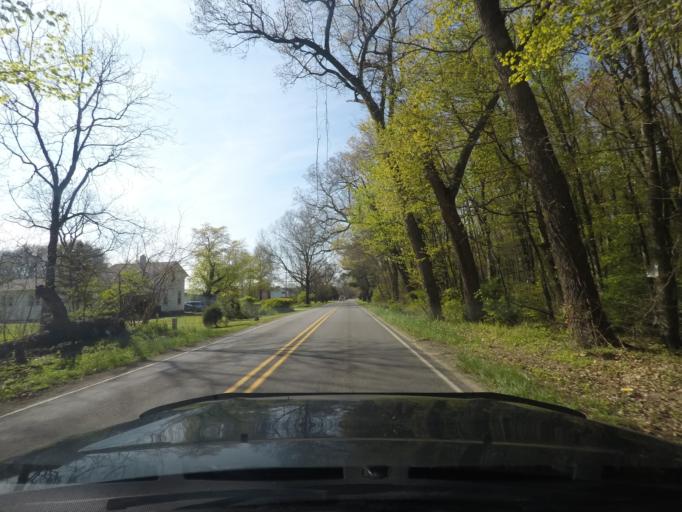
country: US
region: Indiana
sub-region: Elkhart County
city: Elkhart
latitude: 41.7119
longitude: -86.0262
